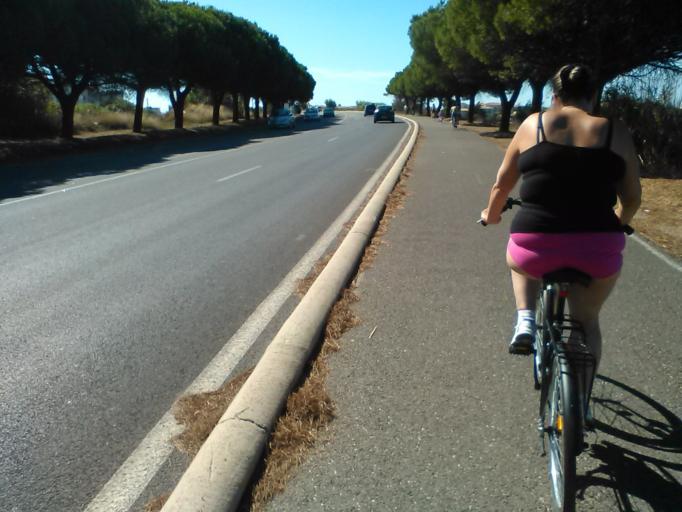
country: FR
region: Languedoc-Roussillon
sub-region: Departement de l'Herault
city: Perols
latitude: 43.5494
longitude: 3.9689
